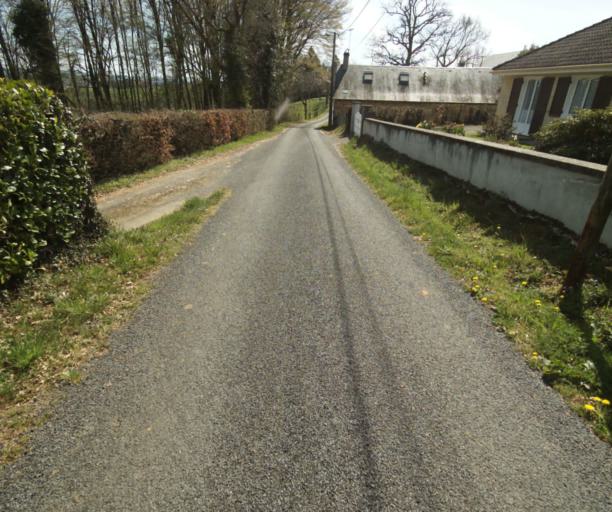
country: FR
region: Limousin
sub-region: Departement de la Correze
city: Seilhac
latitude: 45.3906
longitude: 1.7701
